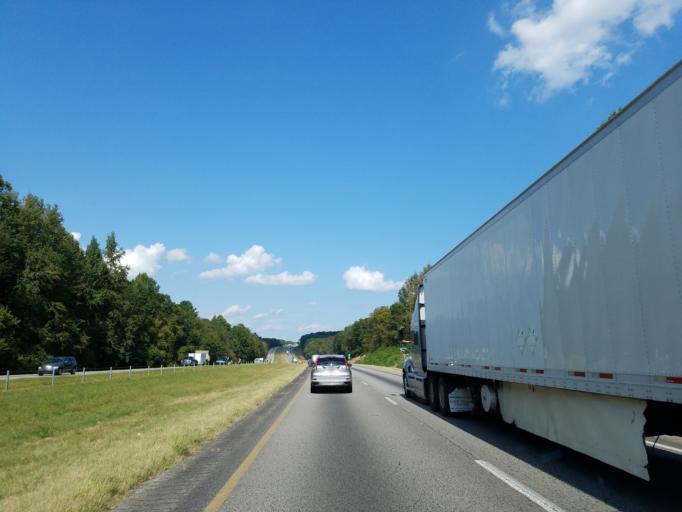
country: US
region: Georgia
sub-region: Jackson County
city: Jefferson
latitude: 34.1660
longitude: -83.6240
